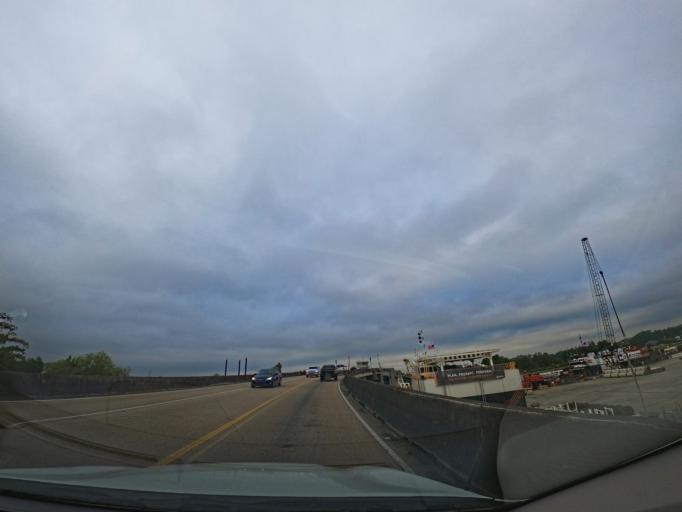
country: US
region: Louisiana
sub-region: Terrebonne Parish
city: Houma
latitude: 29.5673
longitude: -90.7194
